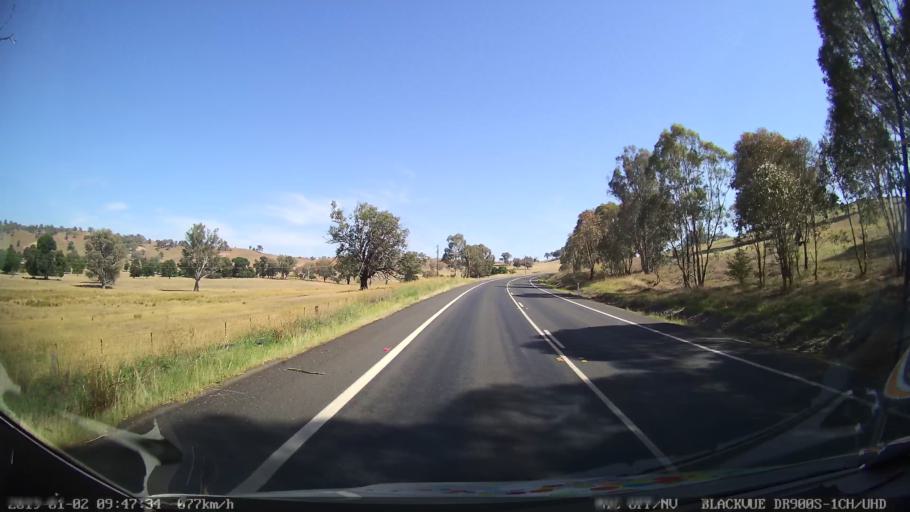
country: AU
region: New South Wales
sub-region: Tumut Shire
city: Tumut
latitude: -35.2833
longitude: 148.2067
